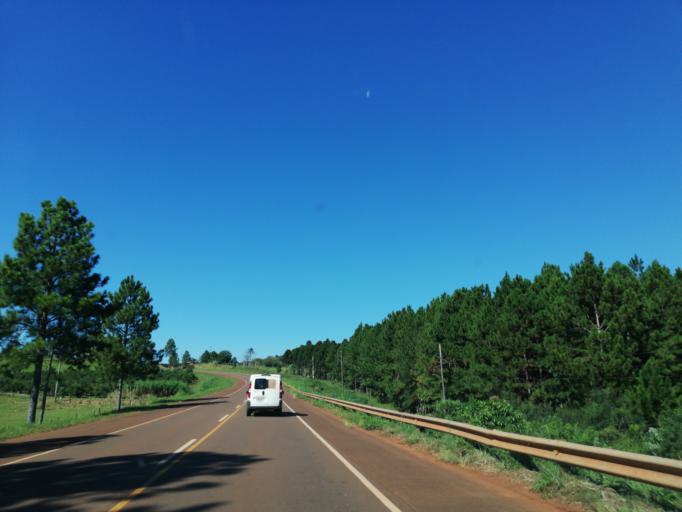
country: AR
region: Misiones
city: Dos de Mayo
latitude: -27.0550
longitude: -54.4297
